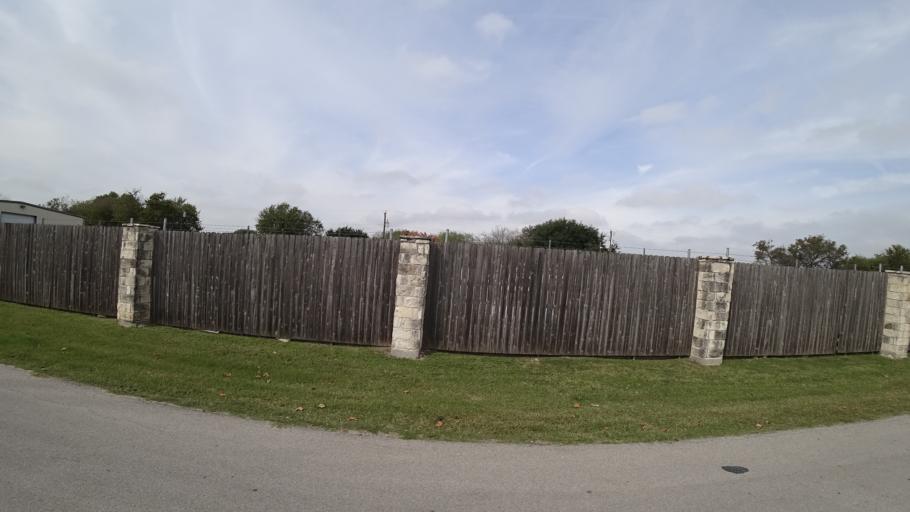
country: US
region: Texas
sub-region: Travis County
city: Wells Branch
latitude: 30.4491
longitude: -97.6691
